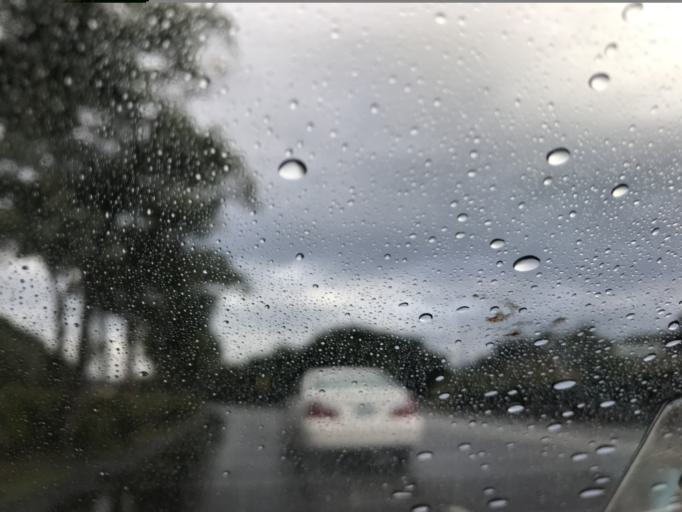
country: TW
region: Taiwan
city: Daxi
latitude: 24.8589
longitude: 121.2228
